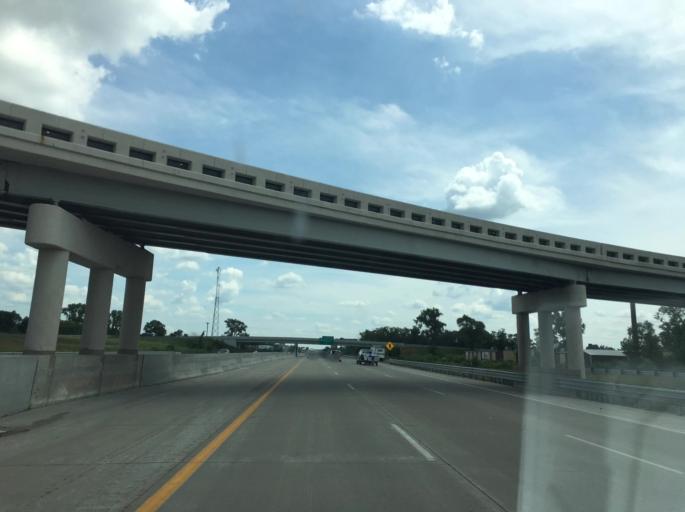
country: US
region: Michigan
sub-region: Saginaw County
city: Buena Vista
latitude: 43.4314
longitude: -83.8909
